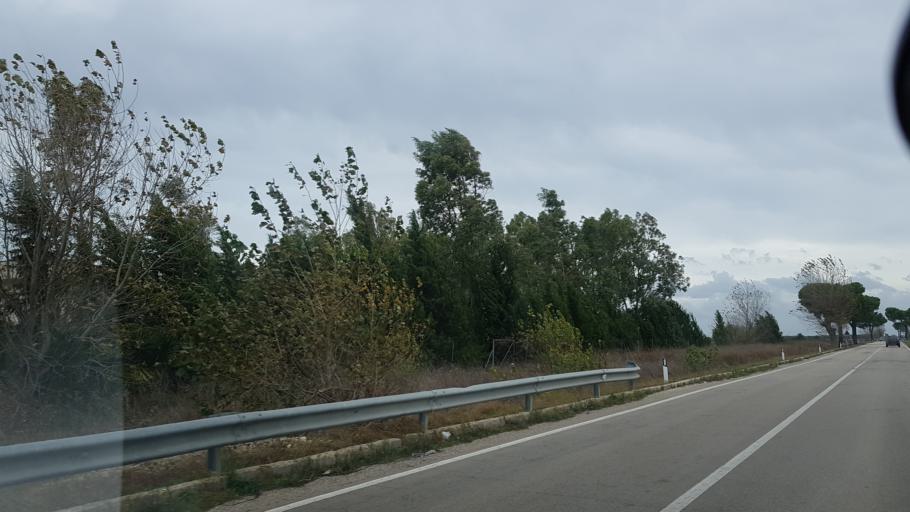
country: IT
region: Apulia
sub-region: Provincia di Brindisi
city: San Pancrazio Salentino
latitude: 40.4121
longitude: 17.8645
